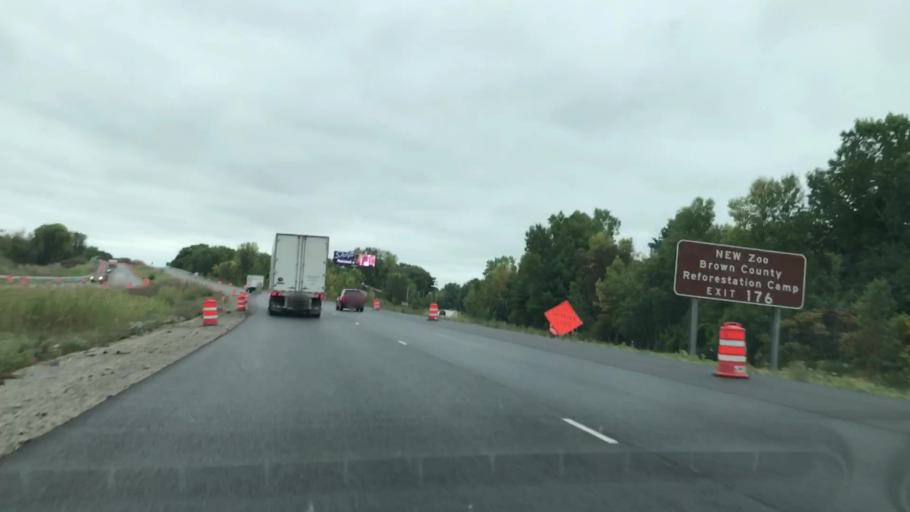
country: US
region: Wisconsin
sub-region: Brown County
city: Suamico
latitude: 44.6462
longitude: -88.0498
